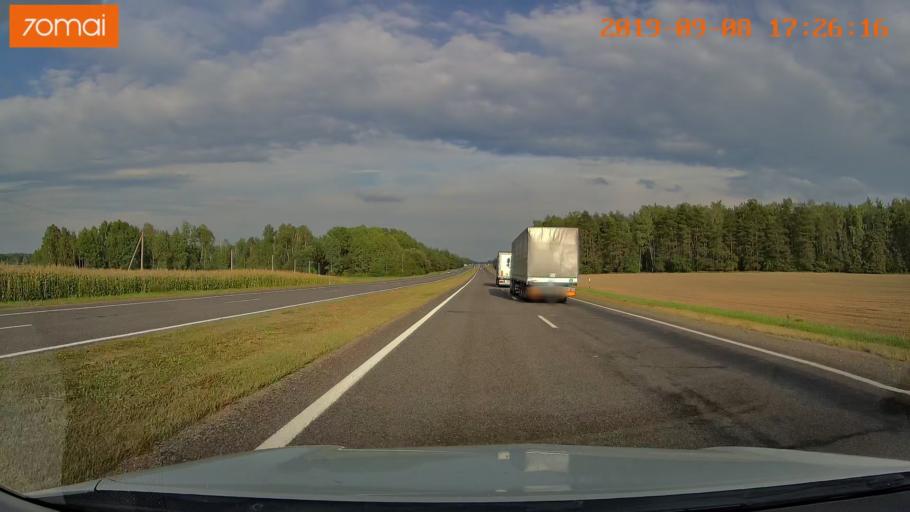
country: BY
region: Grodnenskaya
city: Skidal'
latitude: 53.5761
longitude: 24.3669
